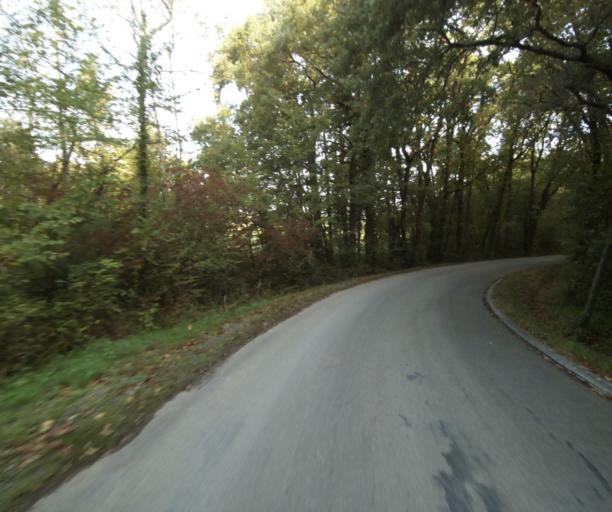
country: FR
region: Midi-Pyrenees
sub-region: Departement de la Haute-Garonne
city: Villemur-sur-Tarn
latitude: 43.9205
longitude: 1.5055
